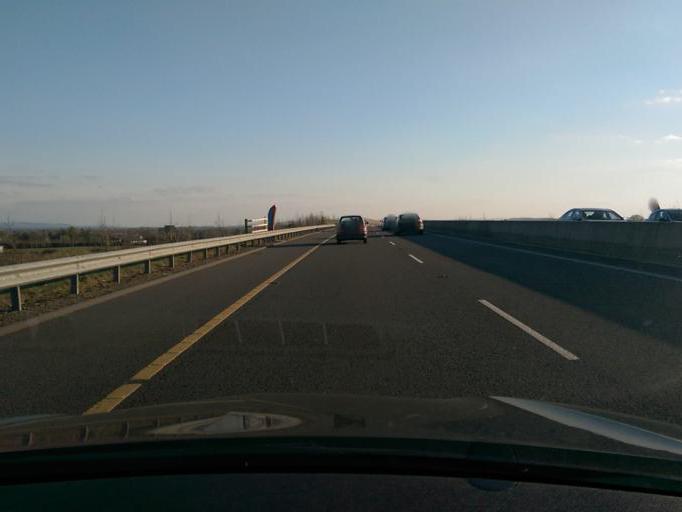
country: IE
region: Leinster
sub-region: Laois
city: Mountrath
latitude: 52.9806
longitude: -7.4324
